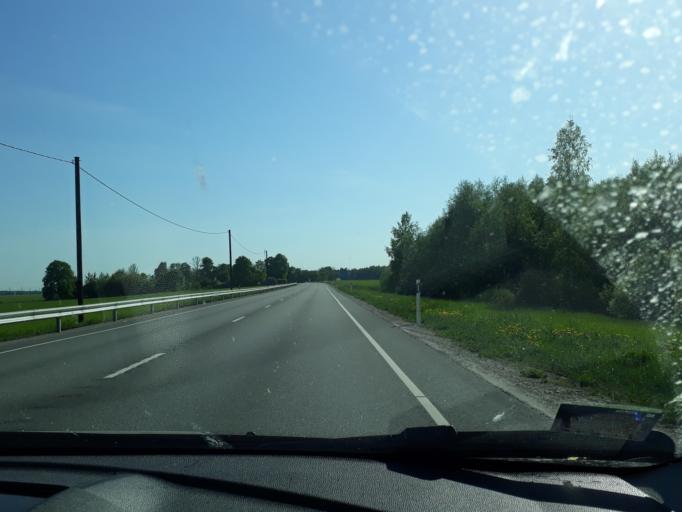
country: EE
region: Paernumaa
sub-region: Tootsi vald
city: Tootsi
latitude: 58.5572
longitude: 24.8612
